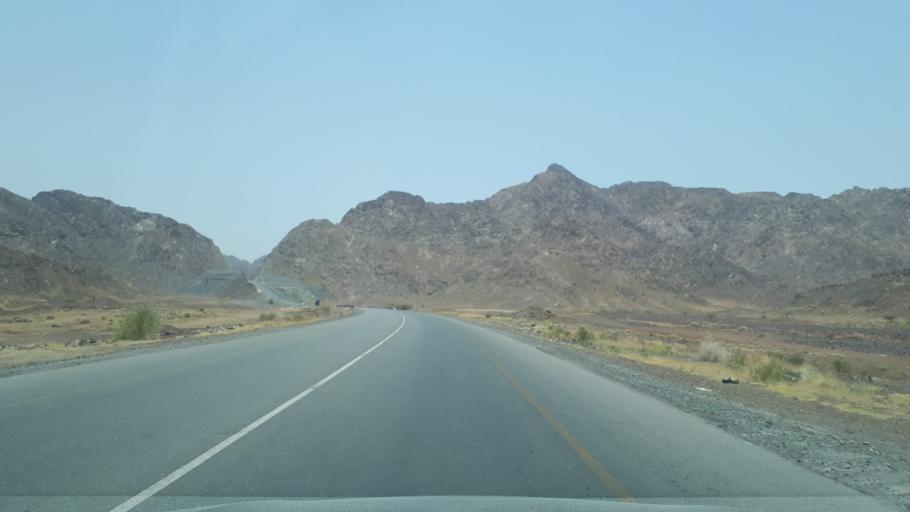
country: OM
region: Al Batinah
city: Rustaq
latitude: 23.4155
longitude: 57.3358
